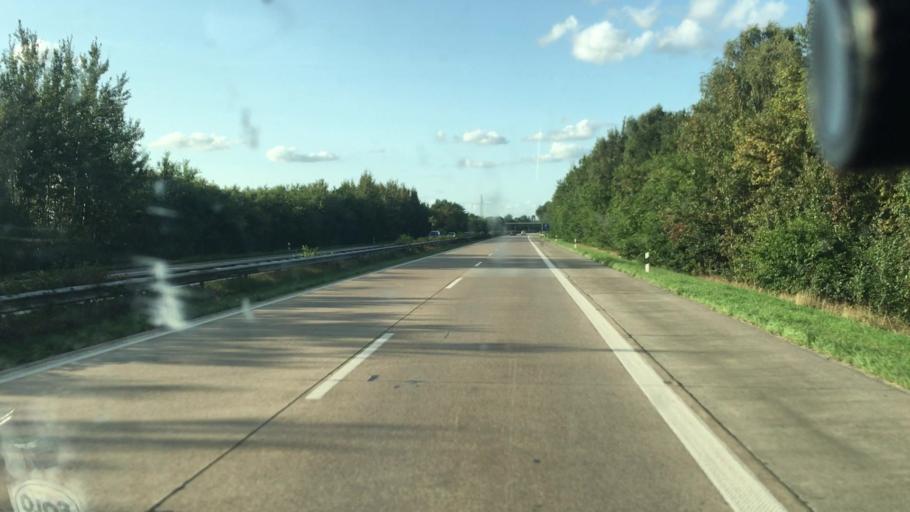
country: DE
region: Lower Saxony
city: Wiefelstede
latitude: 53.3132
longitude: 8.1422
